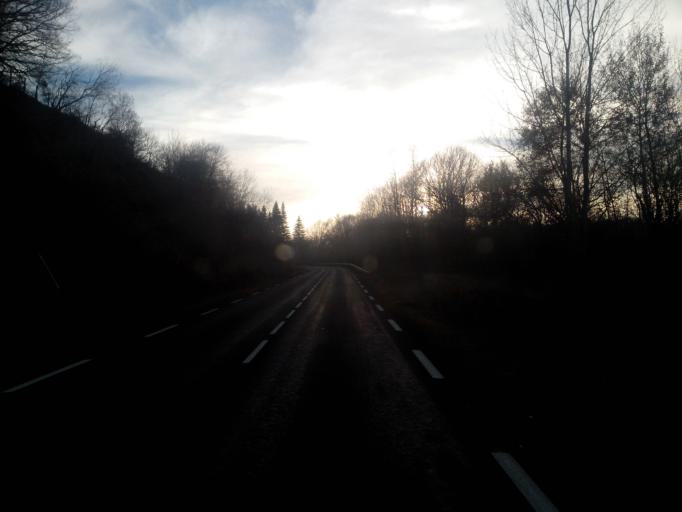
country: FR
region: Auvergne
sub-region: Departement du Cantal
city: Riom-es-Montagnes
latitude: 45.3174
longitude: 2.5971
